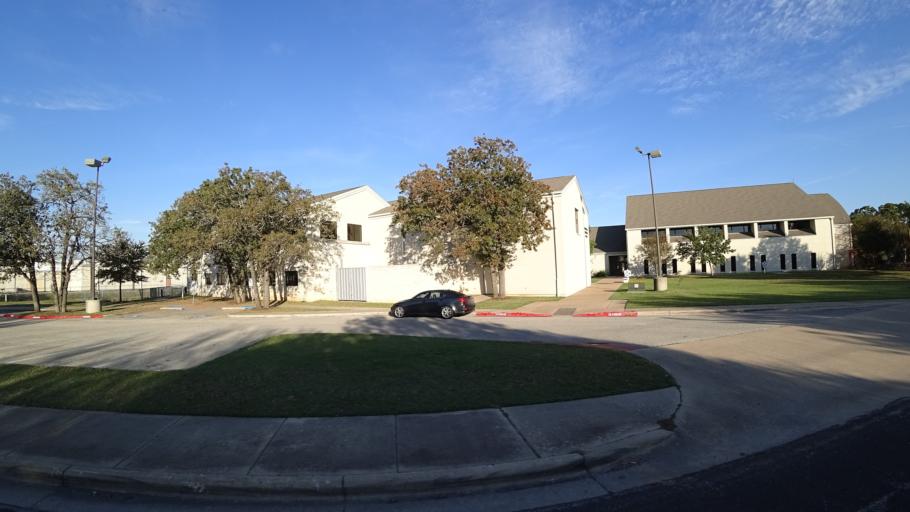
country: US
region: Texas
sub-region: Williamson County
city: Anderson Mill
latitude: 30.4454
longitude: -97.8067
